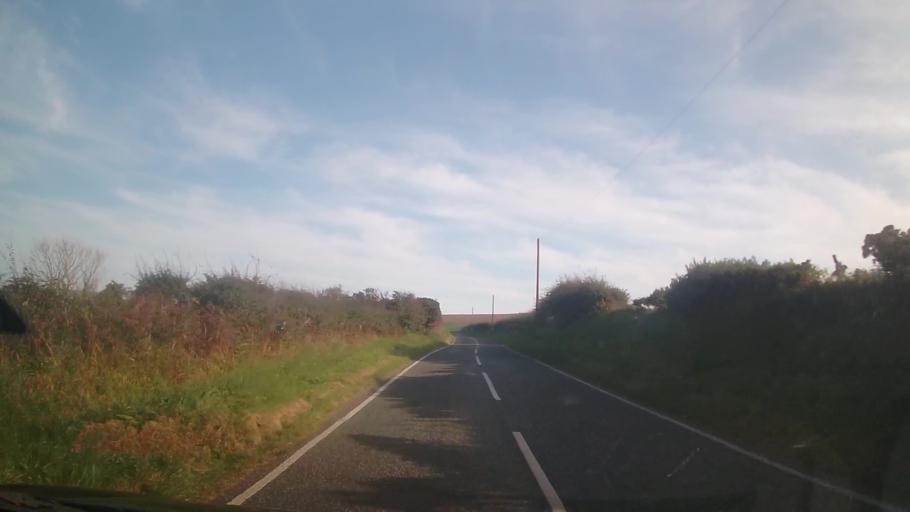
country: GB
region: Wales
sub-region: Pembrokeshire
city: Ambleston
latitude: 51.9689
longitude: -4.9042
